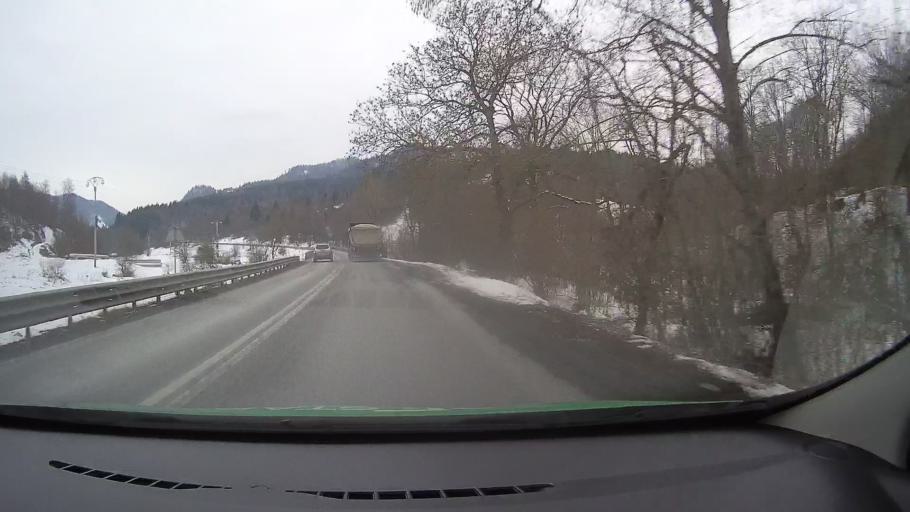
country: RO
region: Brasov
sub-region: Oras Rasnov
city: Rasnov
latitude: 45.5293
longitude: 25.4993
